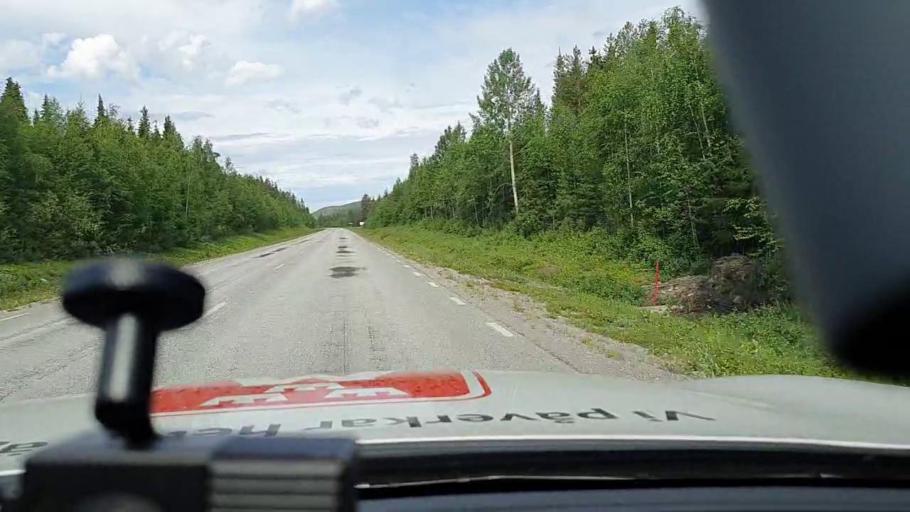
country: SE
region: Norrbotten
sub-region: Jokkmokks Kommun
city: Jokkmokk
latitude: 66.5503
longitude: 20.1221
